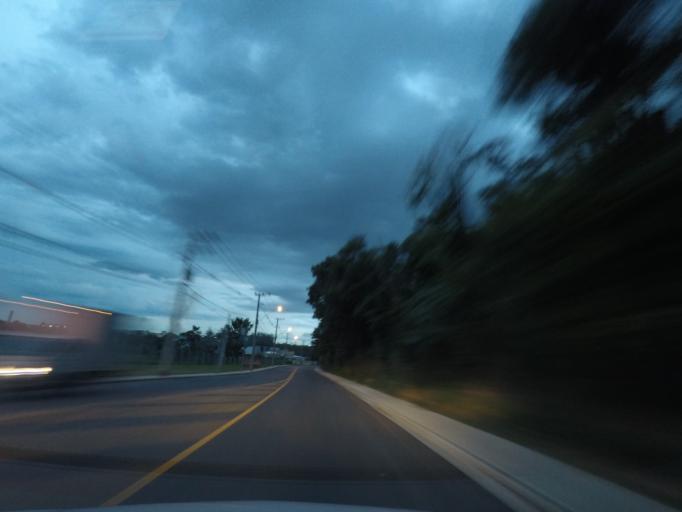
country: BR
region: Sao Paulo
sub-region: Vinhedo
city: Vinhedo
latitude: -23.0548
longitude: -47.0092
